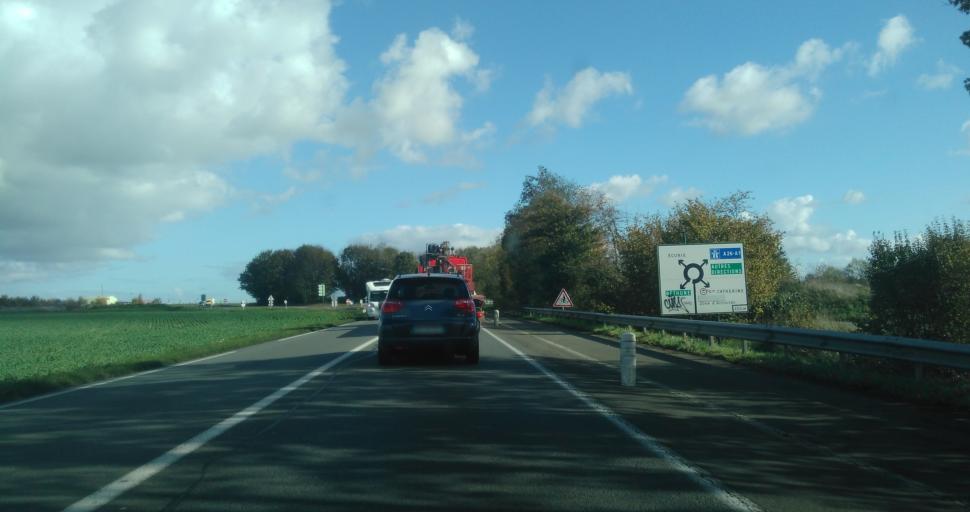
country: FR
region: Nord-Pas-de-Calais
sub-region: Departement du Pas-de-Calais
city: Anzin-Saint-Aubin
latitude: 50.3238
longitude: 2.7539
